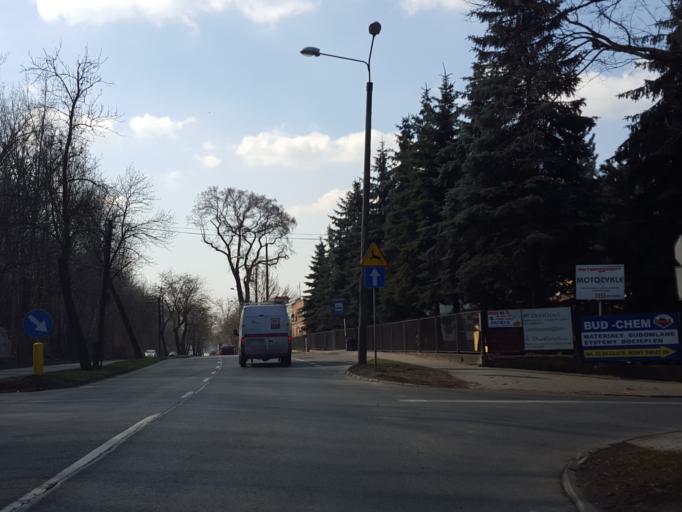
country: PL
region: Silesian Voivodeship
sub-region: Ruda Slaska
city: Ruda Slaska
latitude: 50.2533
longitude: 18.8519
